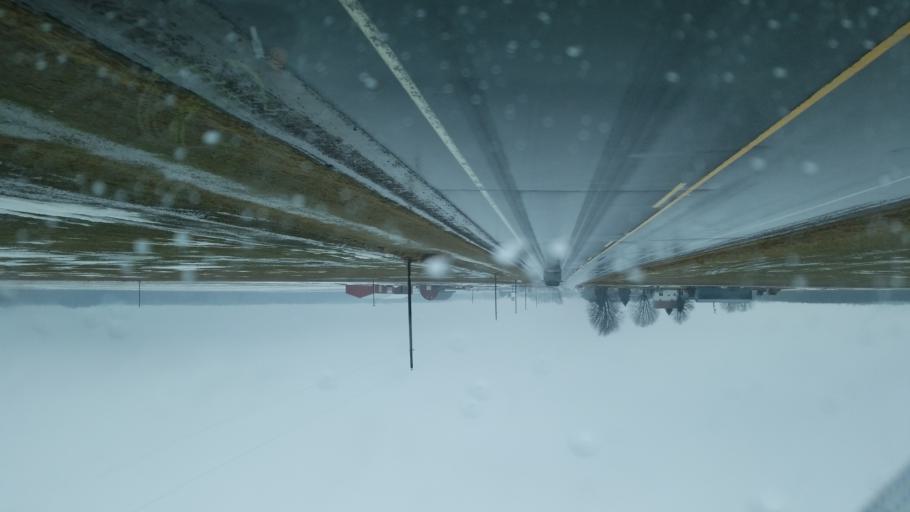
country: US
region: Wisconsin
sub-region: Marathon County
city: Spencer
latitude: 44.6562
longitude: -90.3339
